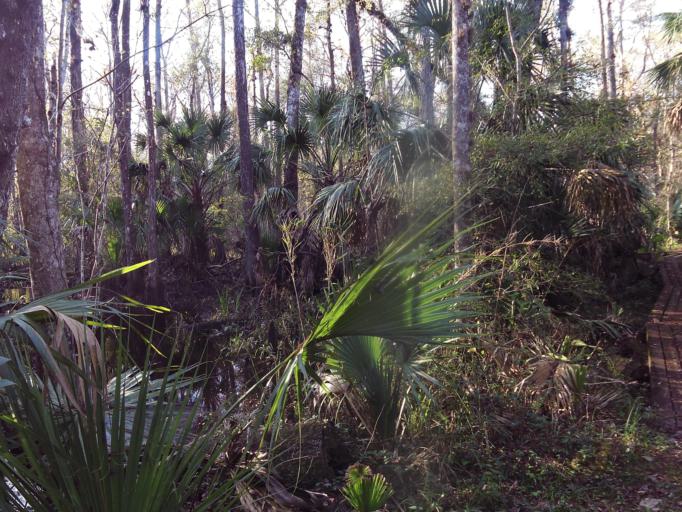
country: US
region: Florida
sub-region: Putnam County
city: Palatka
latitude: 29.6781
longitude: -81.7541
